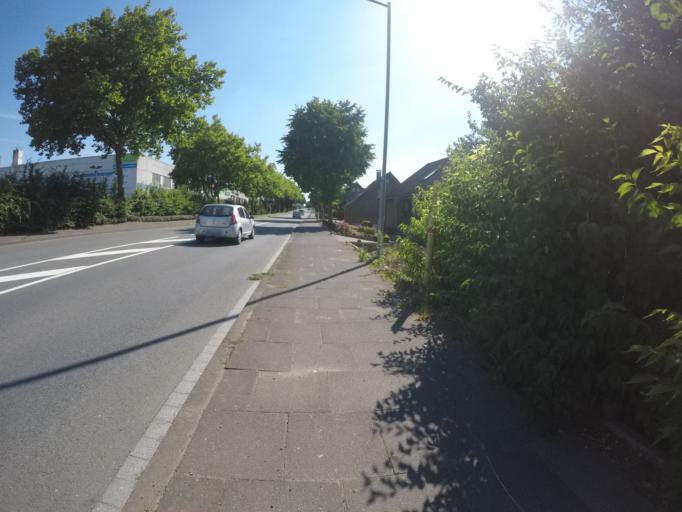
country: DE
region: North Rhine-Westphalia
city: Bad Oeynhausen
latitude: 52.1834
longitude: 8.7576
